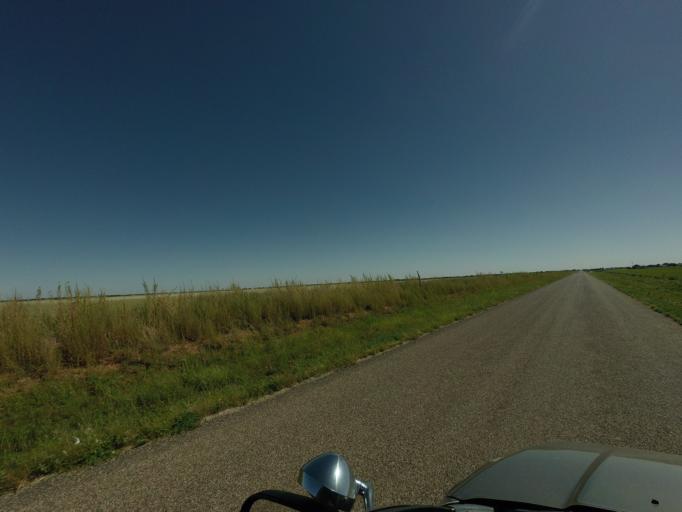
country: US
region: New Mexico
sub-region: Curry County
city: Clovis
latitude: 34.4457
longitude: -103.2317
